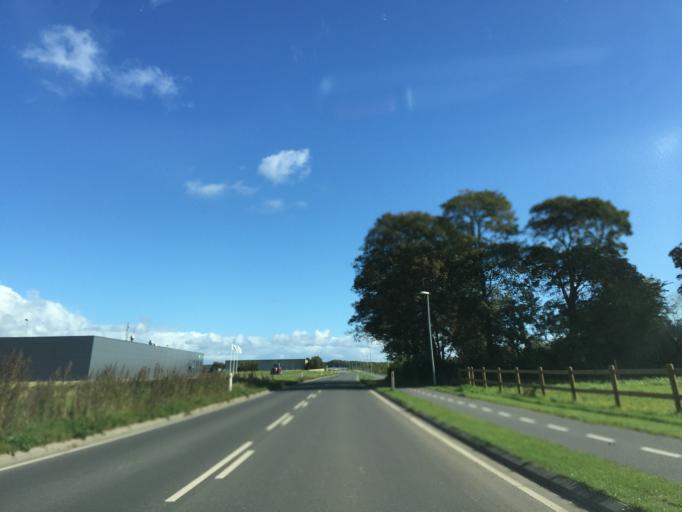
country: DK
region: Central Jutland
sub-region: Viborg Kommune
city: Bjerringbro
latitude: 56.3950
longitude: 9.6613
